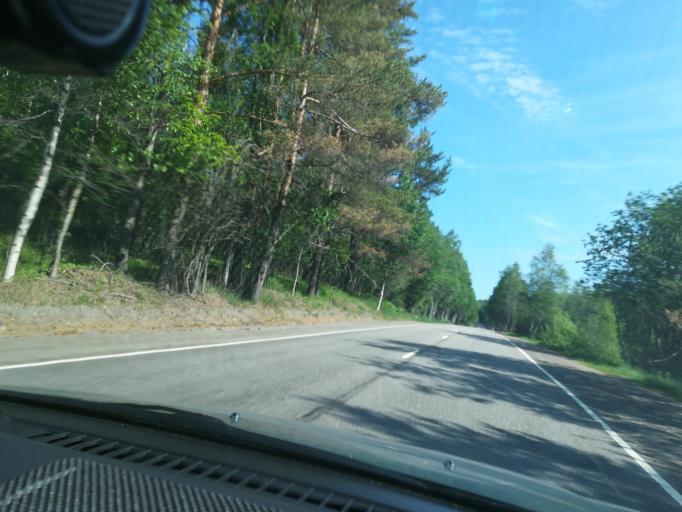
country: RU
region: Leningrad
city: Lesogorskiy
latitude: 60.9613
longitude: 28.9056
